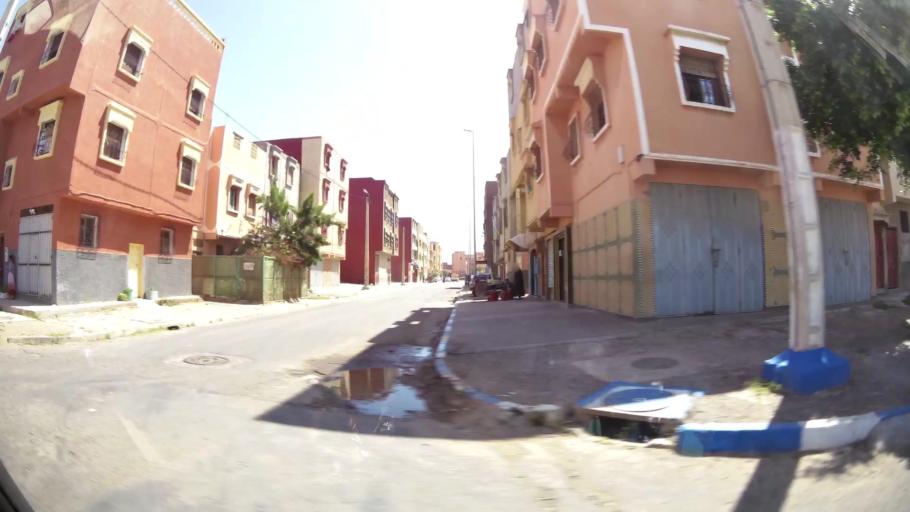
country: MA
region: Souss-Massa-Draa
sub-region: Inezgane-Ait Mellou
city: Inezgane
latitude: 30.3281
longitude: -9.5002
